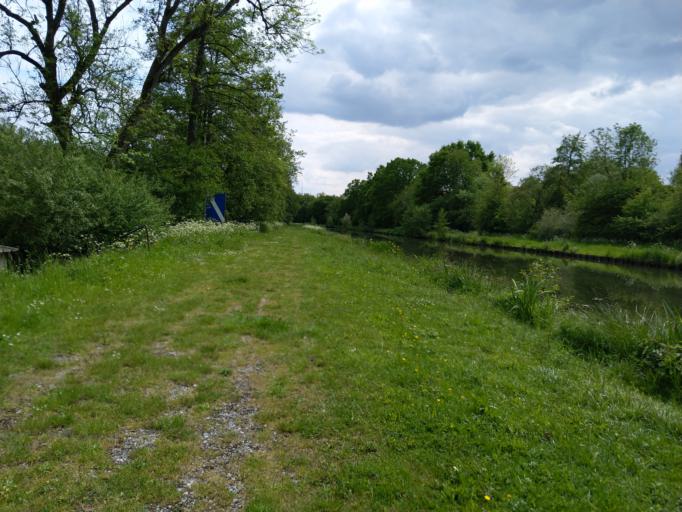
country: FR
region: Picardie
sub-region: Departement de l'Aisne
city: Wassigny
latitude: 50.0465
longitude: 3.6435
